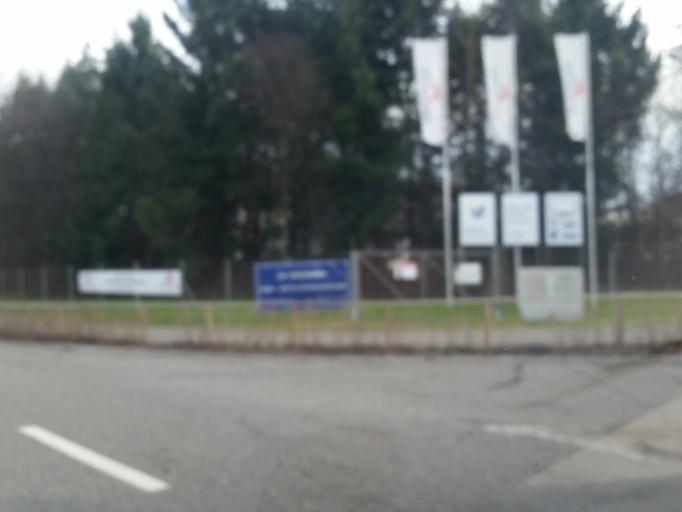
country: CH
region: Aargau
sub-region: Bezirk Bremgarten
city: Villmergen
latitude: 47.3522
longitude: 8.2534
